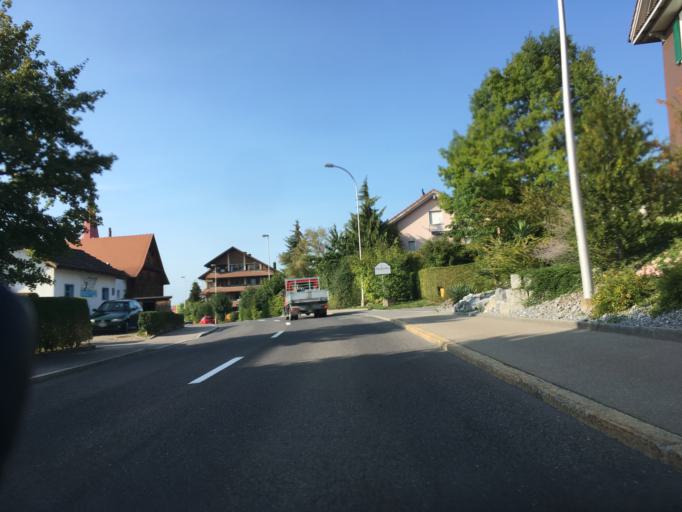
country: CH
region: Zug
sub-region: Zug
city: Hunenberg
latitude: 47.1539
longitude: 8.4403
